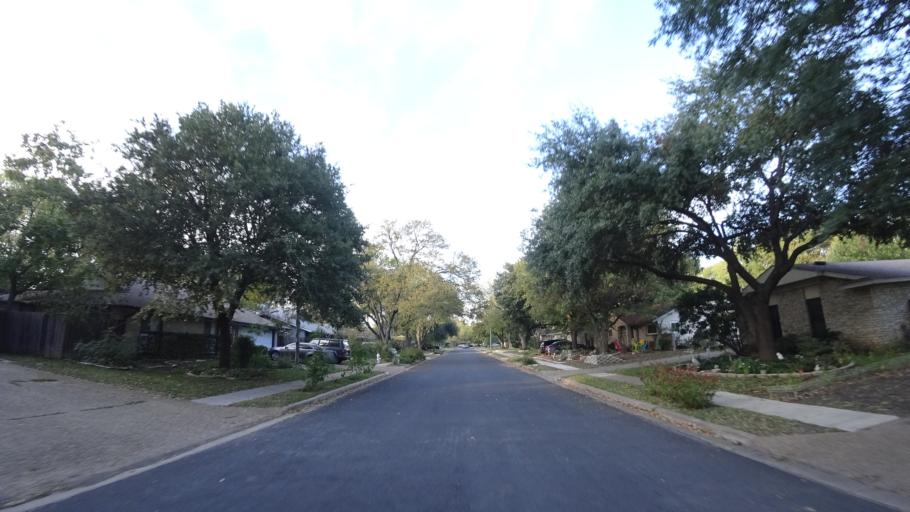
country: US
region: Texas
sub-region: Williamson County
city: Jollyville
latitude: 30.3680
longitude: -97.7368
